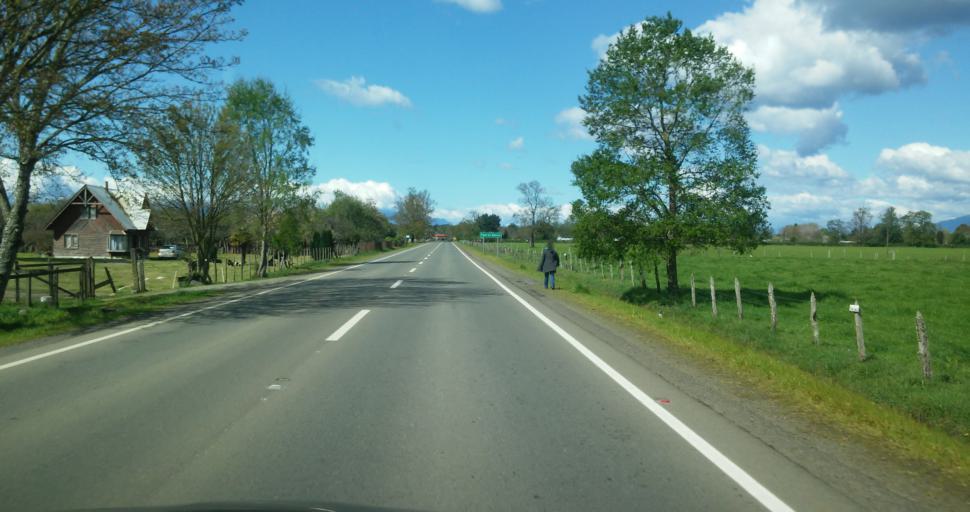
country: CL
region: Los Rios
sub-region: Provincia del Ranco
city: Rio Bueno
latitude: -40.2400
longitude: -72.6011
